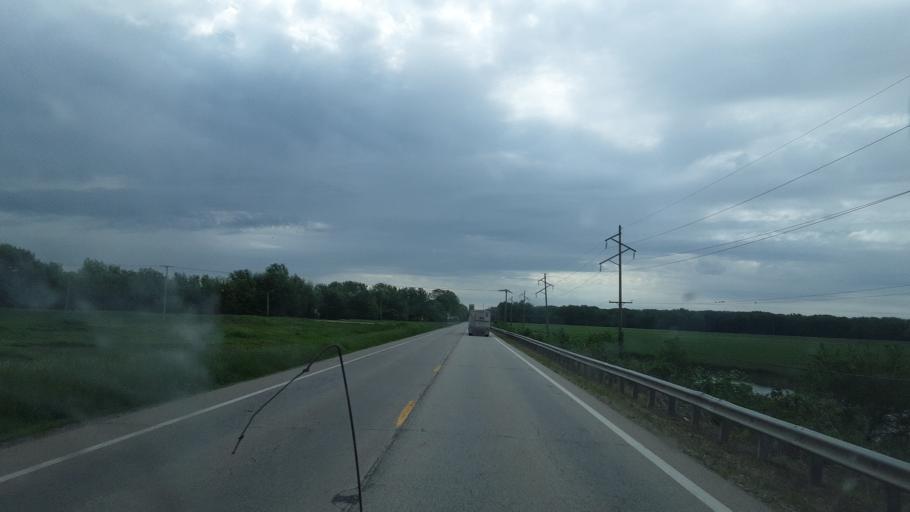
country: US
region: Illinois
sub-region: Mason County
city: Havana
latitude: 40.2971
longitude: -90.0874
